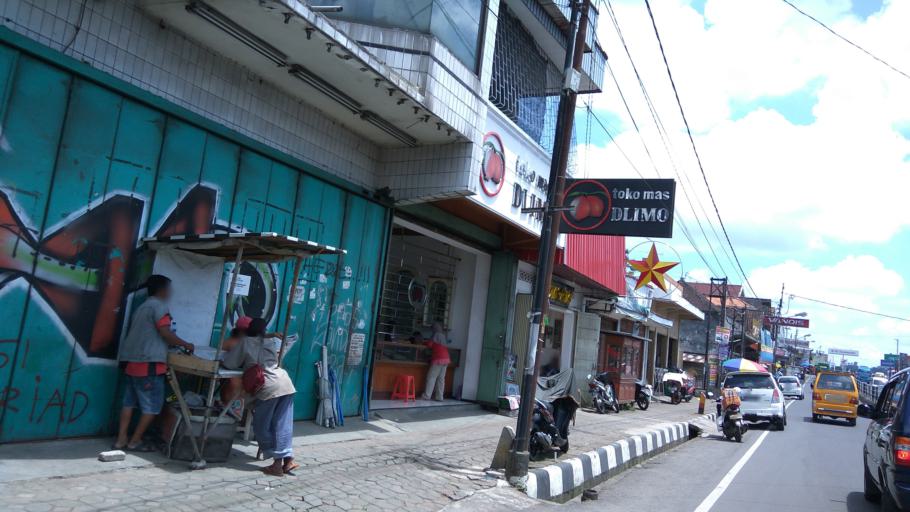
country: ID
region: Central Java
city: Ambarawa
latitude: -7.2557
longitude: 110.4073
